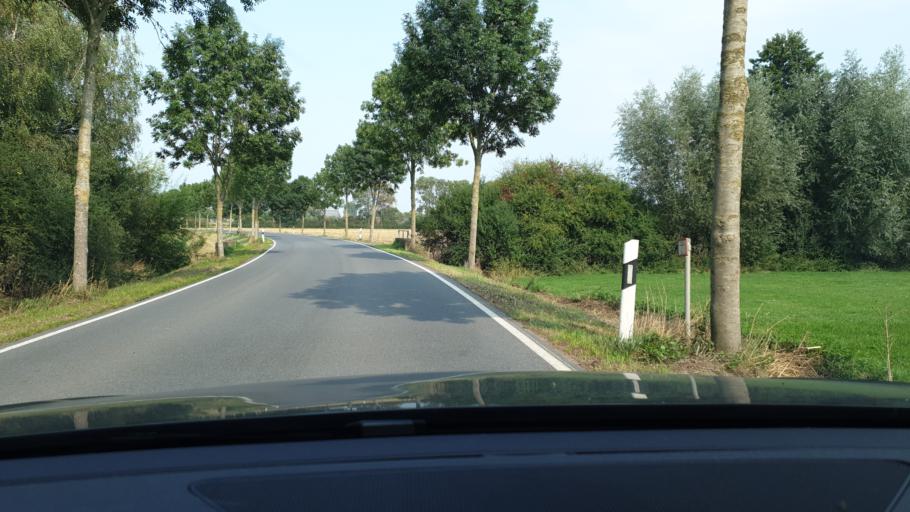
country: DE
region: North Rhine-Westphalia
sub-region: Regierungsbezirk Dusseldorf
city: Kranenburg
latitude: 51.8196
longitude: 6.0179
